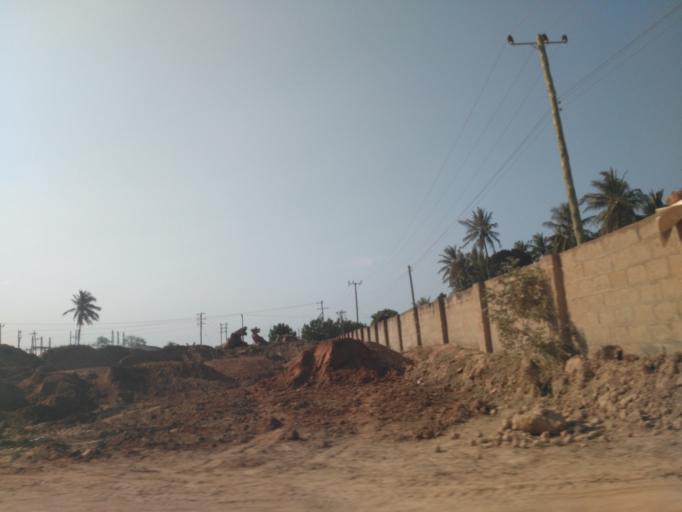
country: TZ
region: Dar es Salaam
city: Dar es Salaam
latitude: -6.8439
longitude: 39.3191
